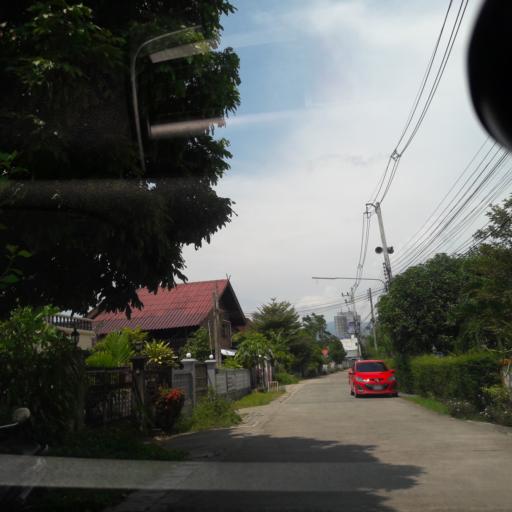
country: TH
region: Chiang Mai
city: San Sai
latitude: 18.8230
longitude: 99.0463
